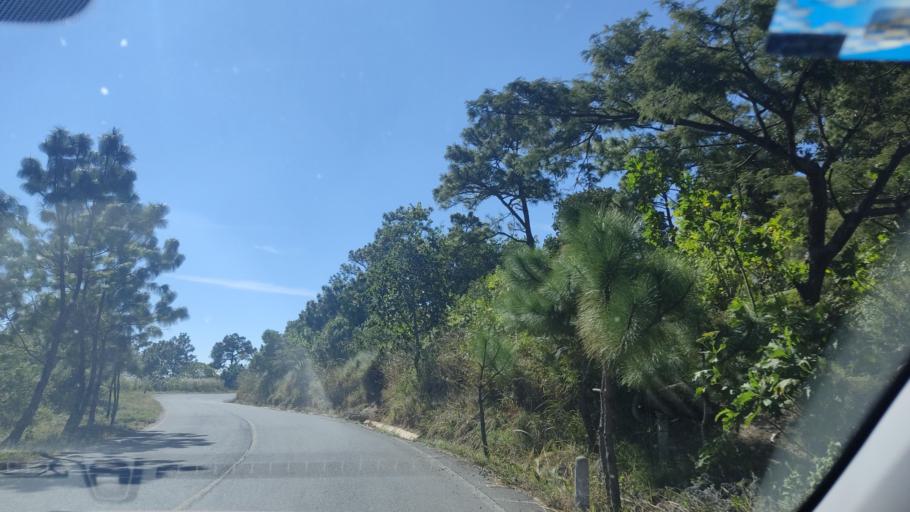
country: MX
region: Nayarit
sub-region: Jala
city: Rosa Blanca
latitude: 21.0978
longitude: -104.3793
